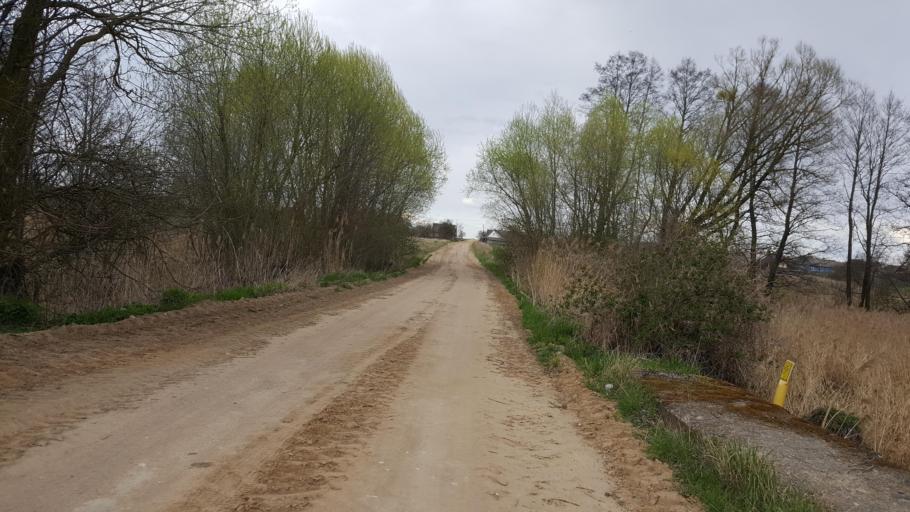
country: BY
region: Brest
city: Kamyanyets
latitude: 52.3959
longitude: 23.7557
